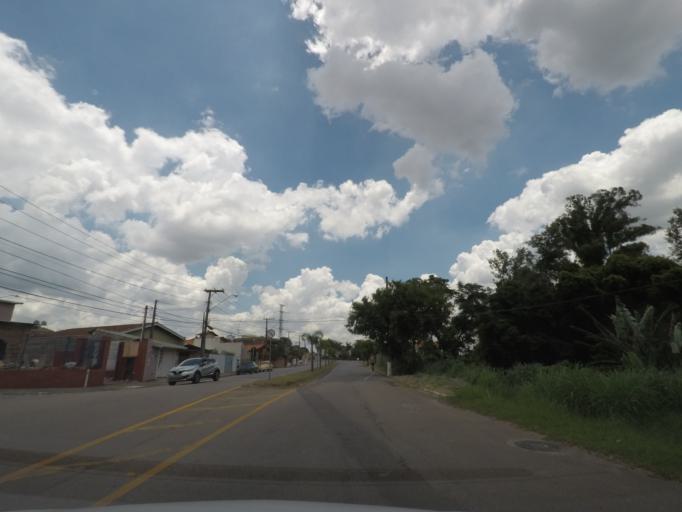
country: BR
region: Sao Paulo
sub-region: Vinhedo
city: Vinhedo
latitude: -23.0388
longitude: -46.9698
